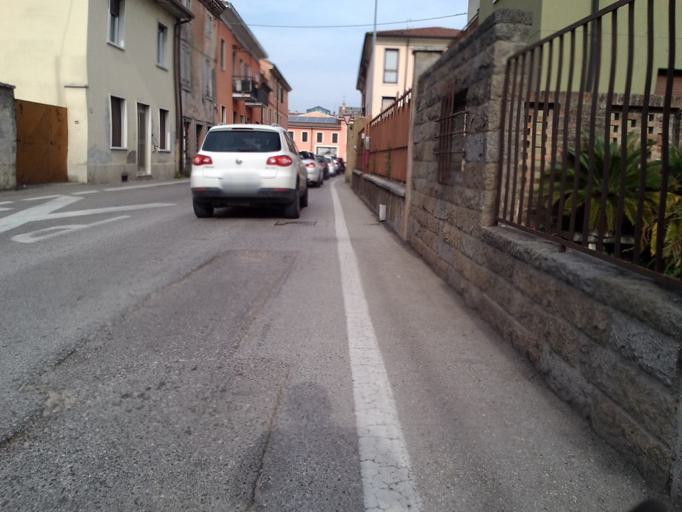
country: IT
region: Veneto
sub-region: Provincia di Verona
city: Villafranca di Verona
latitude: 45.3514
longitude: 10.8497
